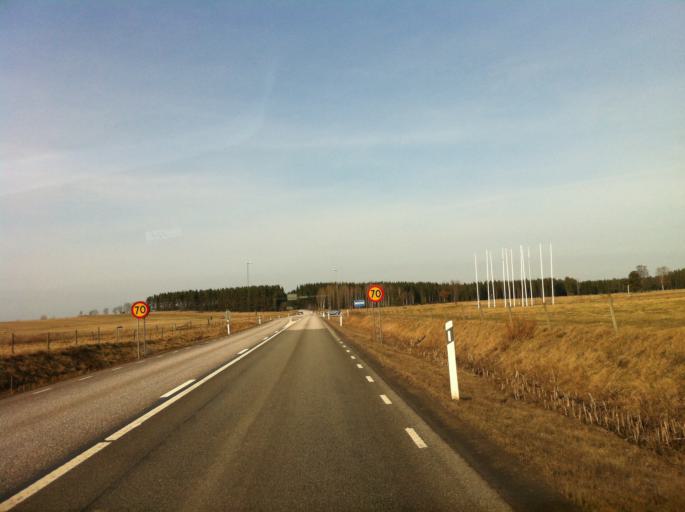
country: SE
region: Vaestra Goetaland
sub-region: Tidaholms Kommun
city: Tidaholm
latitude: 58.1923
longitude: 13.8937
